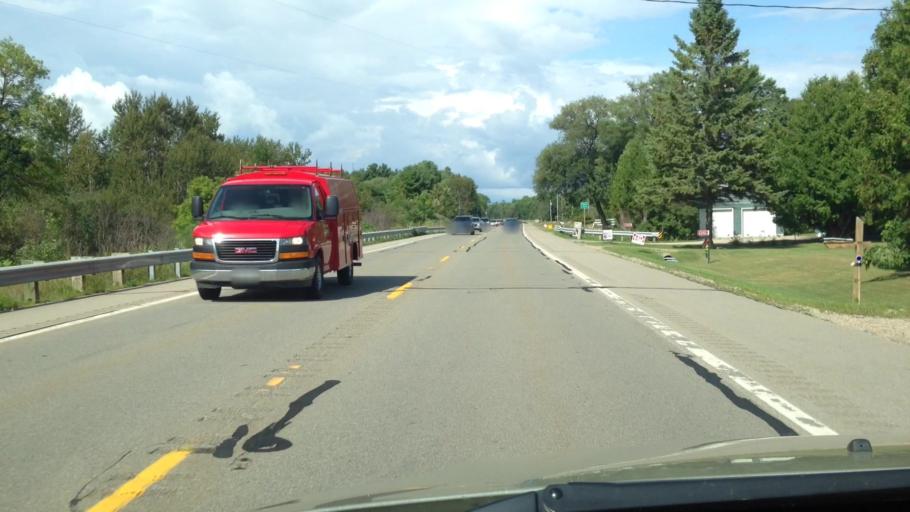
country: US
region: Michigan
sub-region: Menominee County
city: Menominee
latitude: 45.2548
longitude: -87.4833
